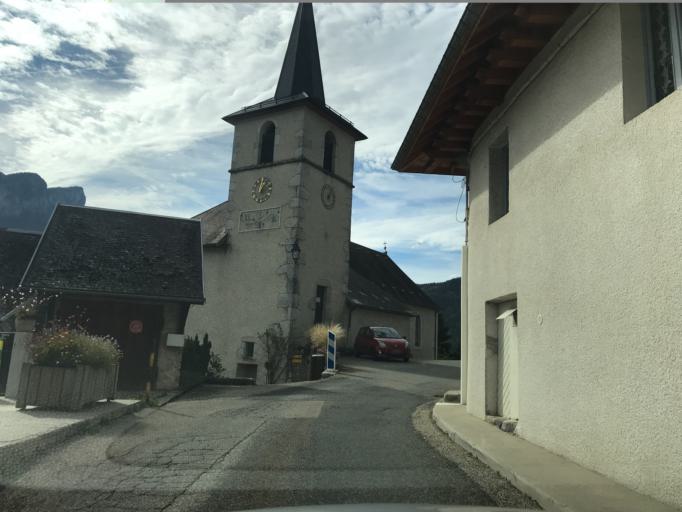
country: FR
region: Rhone-Alpes
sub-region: Departement de la Savoie
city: Les Echelles
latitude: 45.4293
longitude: 5.8248
